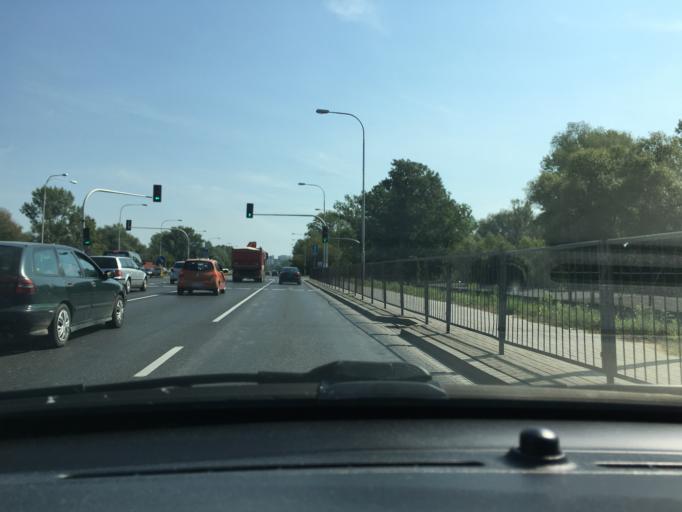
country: PL
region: Masovian Voivodeship
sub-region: Warszawa
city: Praga Poludnie
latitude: 52.2215
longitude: 21.0701
